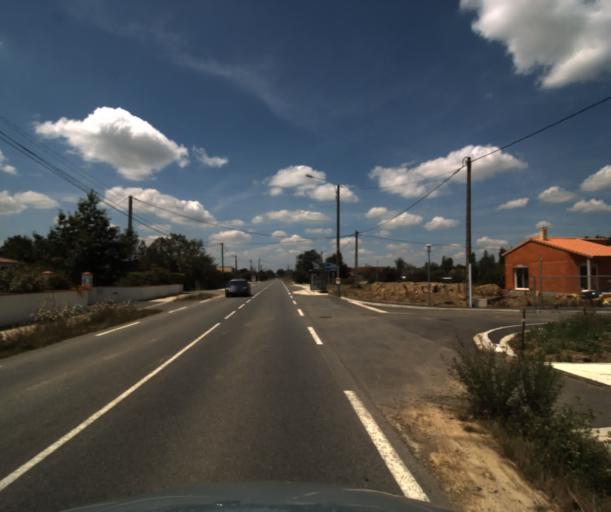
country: FR
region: Midi-Pyrenees
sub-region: Departement de la Haute-Garonne
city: Labastidette
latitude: 43.4673
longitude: 1.2472
